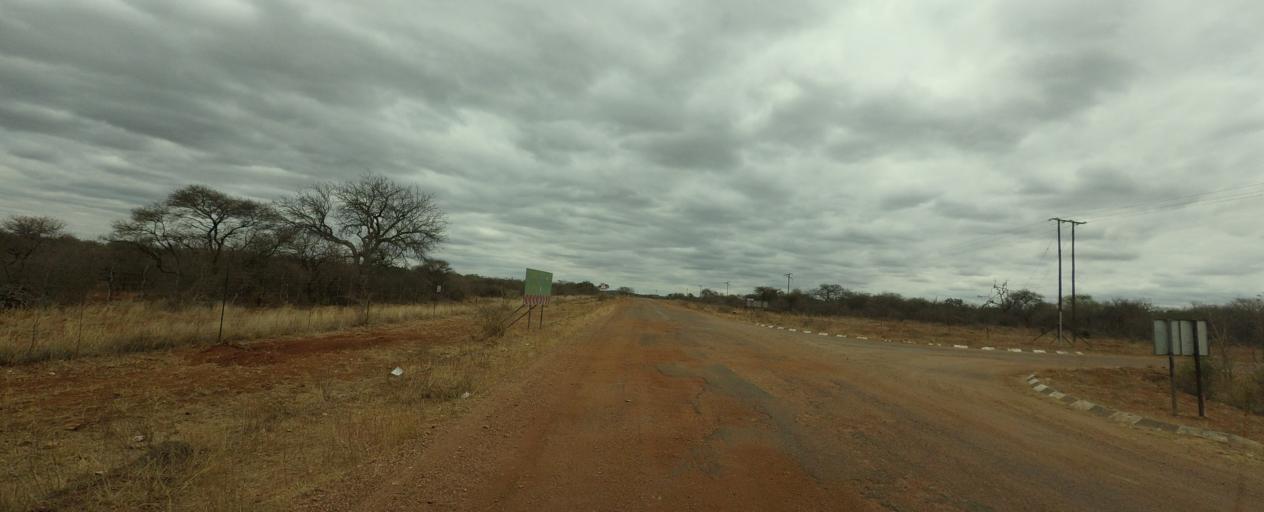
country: BW
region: Central
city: Mathathane
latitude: -22.7390
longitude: 28.4633
